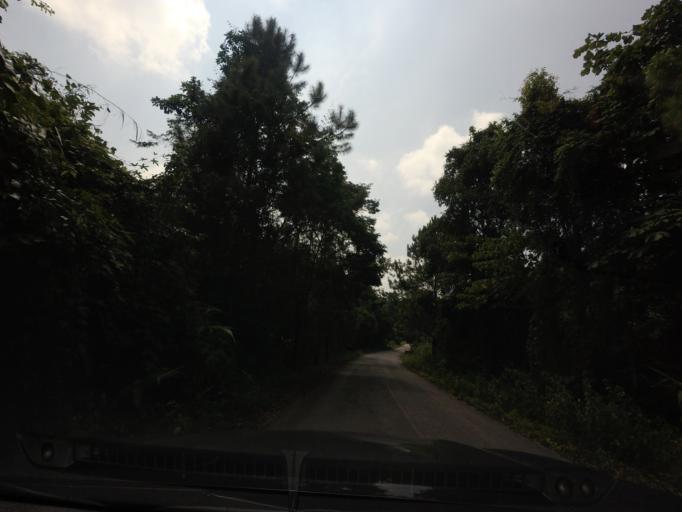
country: TH
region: Loei
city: Na Haeo
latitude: 17.4854
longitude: 100.9395
